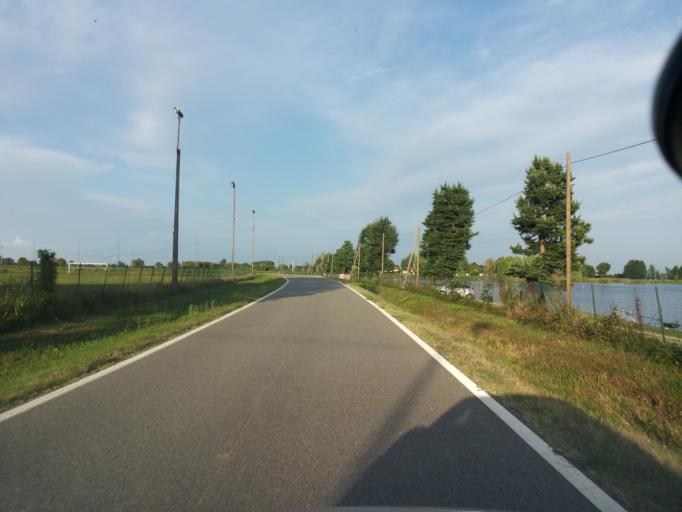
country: IT
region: Piedmont
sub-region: Provincia di Vercelli
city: Salasco
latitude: 45.3249
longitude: 8.2519
